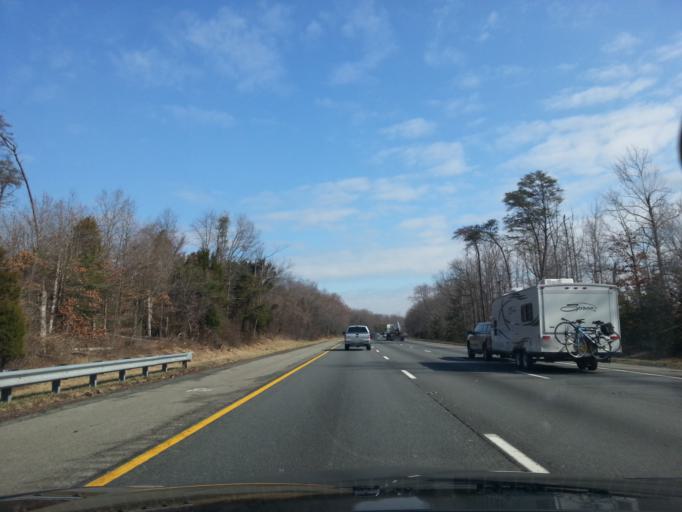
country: US
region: Virginia
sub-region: Stafford County
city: Stafford
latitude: 38.4092
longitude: -77.4297
